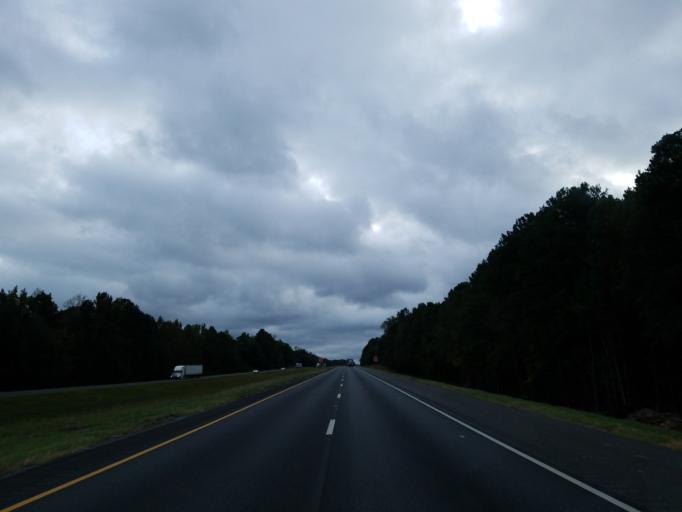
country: US
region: Alabama
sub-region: Hale County
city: Moundville
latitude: 33.0747
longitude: -87.6897
